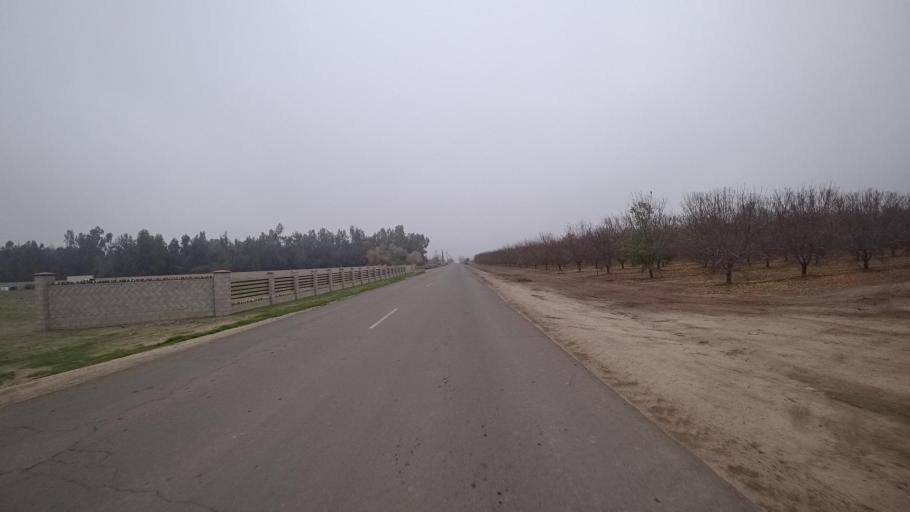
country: US
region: California
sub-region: Kern County
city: Greenfield
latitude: 35.2380
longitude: -119.0843
